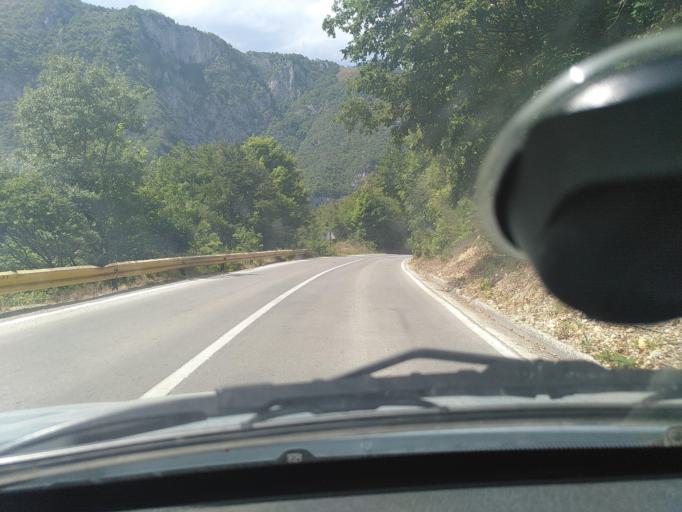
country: ME
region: Opstina Pluzine
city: Pluzine
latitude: 43.2200
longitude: 18.8507
